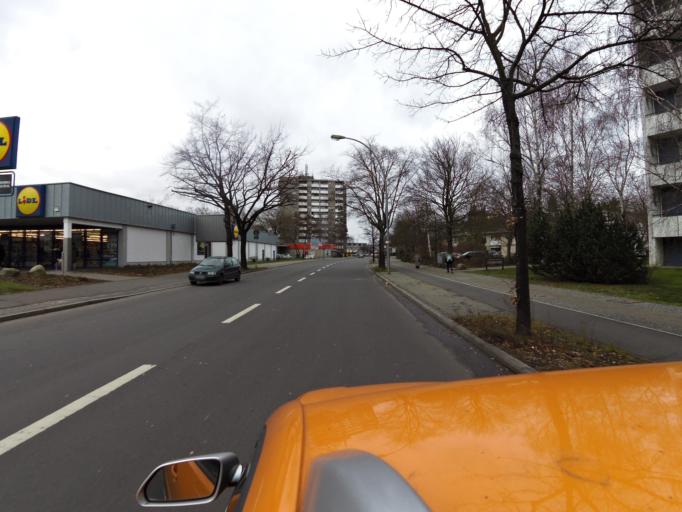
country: DE
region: Berlin
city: Britz
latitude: 52.4394
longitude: 13.4376
